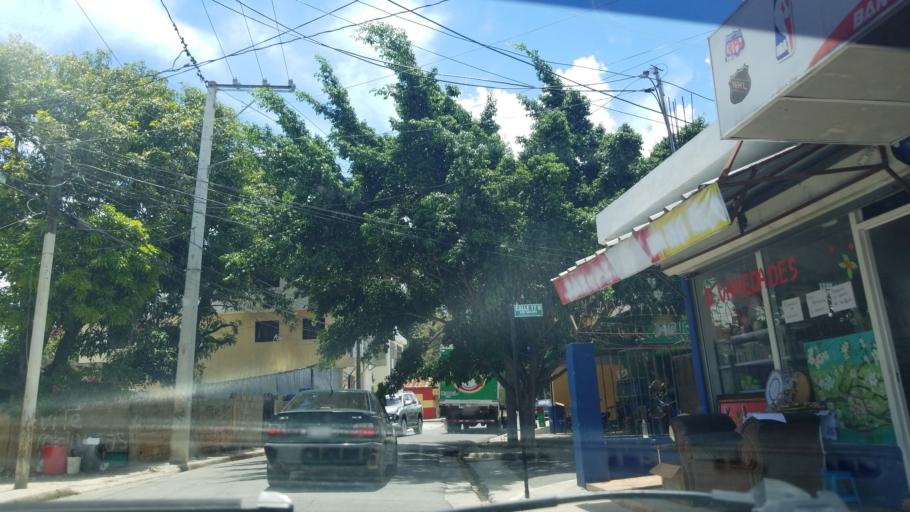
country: DO
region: Santiago
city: Santiago de los Caballeros
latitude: 19.4858
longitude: -70.6797
